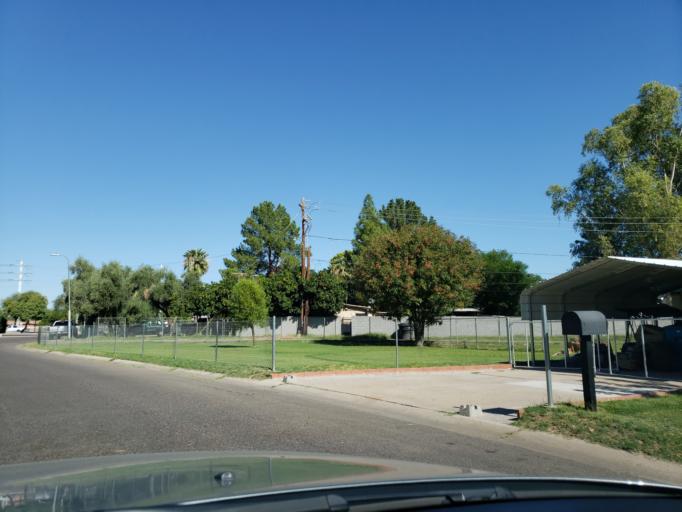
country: US
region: Arizona
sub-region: Maricopa County
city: Glendale
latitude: 33.4868
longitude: -112.1597
